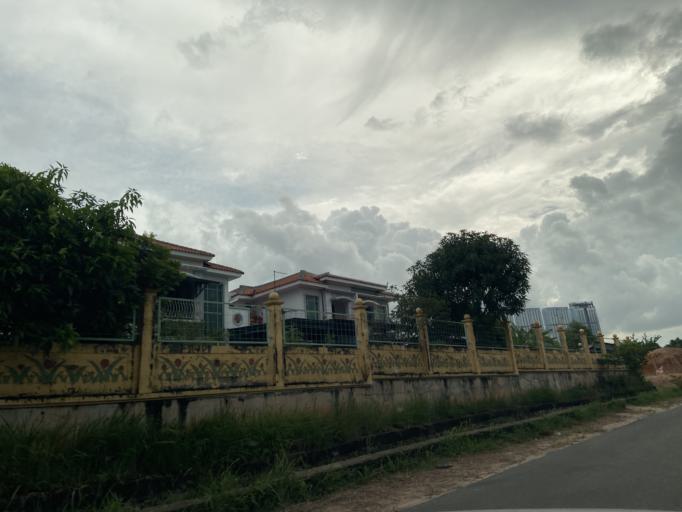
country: SG
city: Singapore
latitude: 1.1239
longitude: 104.0546
